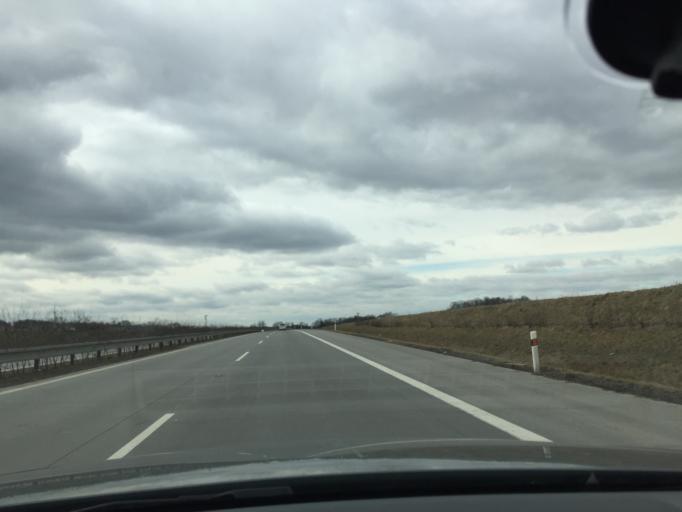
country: CZ
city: Staric
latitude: 49.6642
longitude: 18.2831
